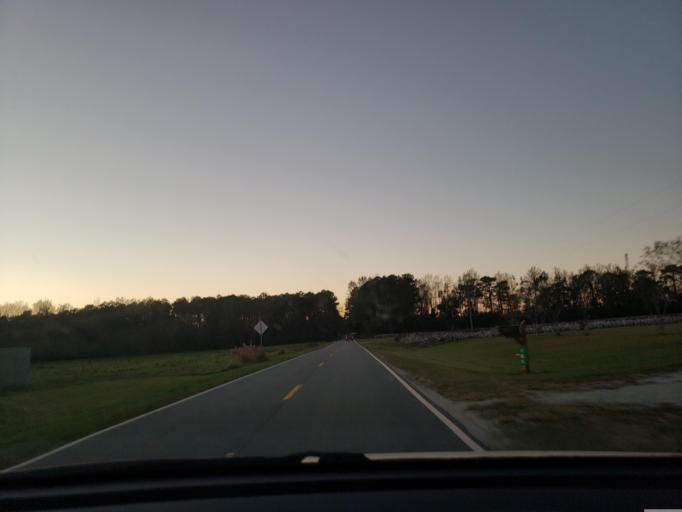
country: US
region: North Carolina
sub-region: Duplin County
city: Beulaville
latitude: 34.7953
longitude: -77.7707
